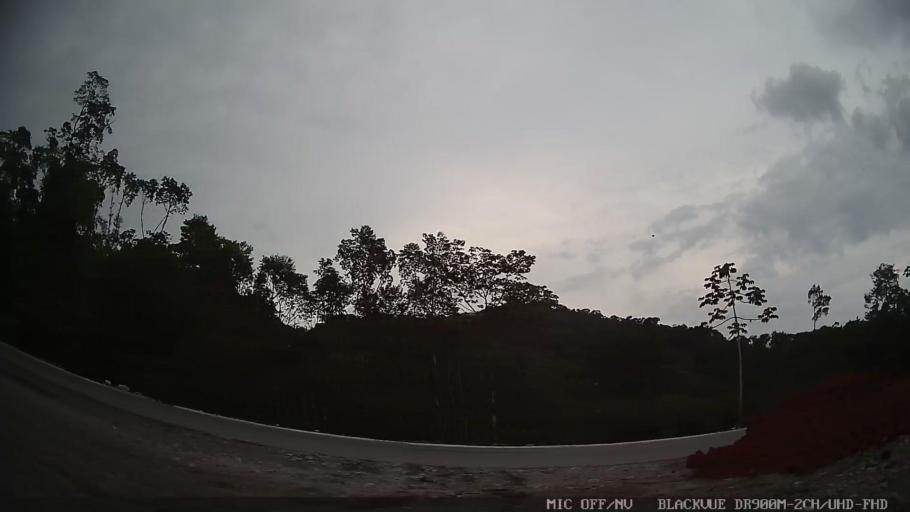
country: BR
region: Sao Paulo
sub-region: Caraguatatuba
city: Caraguatatuba
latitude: -23.5818
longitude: -45.4590
